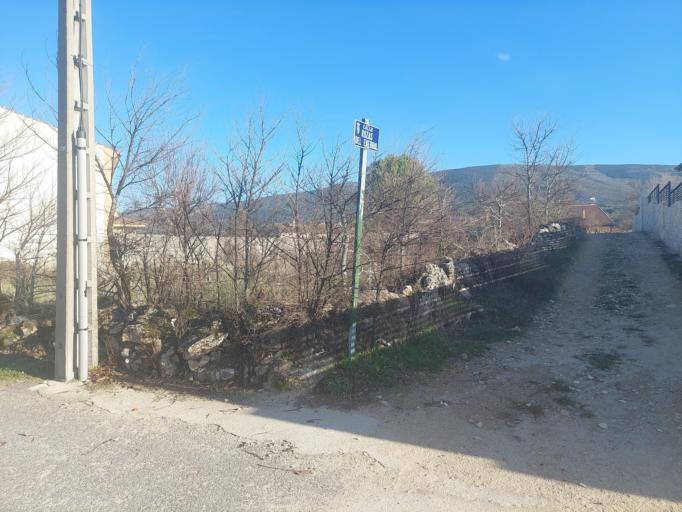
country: ES
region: Castille and Leon
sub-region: Provincia de Segovia
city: Pradena
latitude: 41.1371
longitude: -3.6923
